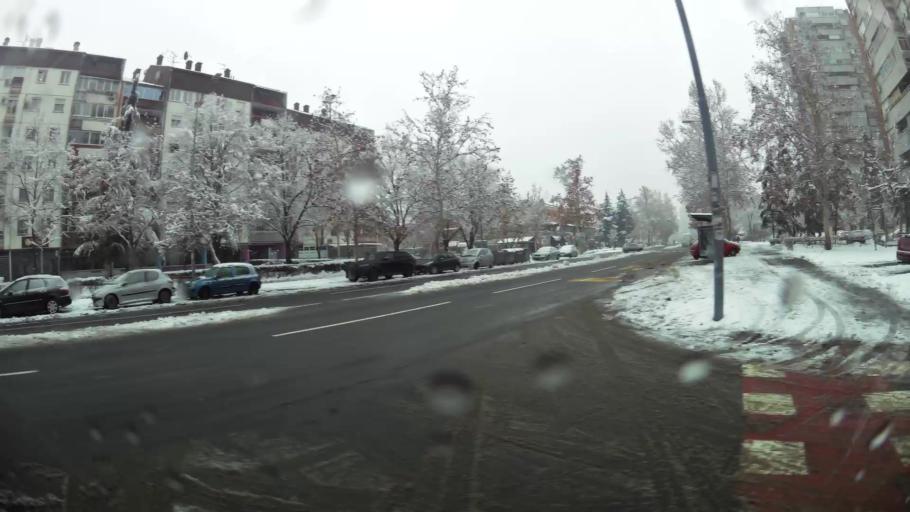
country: RS
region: Central Serbia
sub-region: Belgrade
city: Novi Beograd
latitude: 44.8008
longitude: 20.3890
